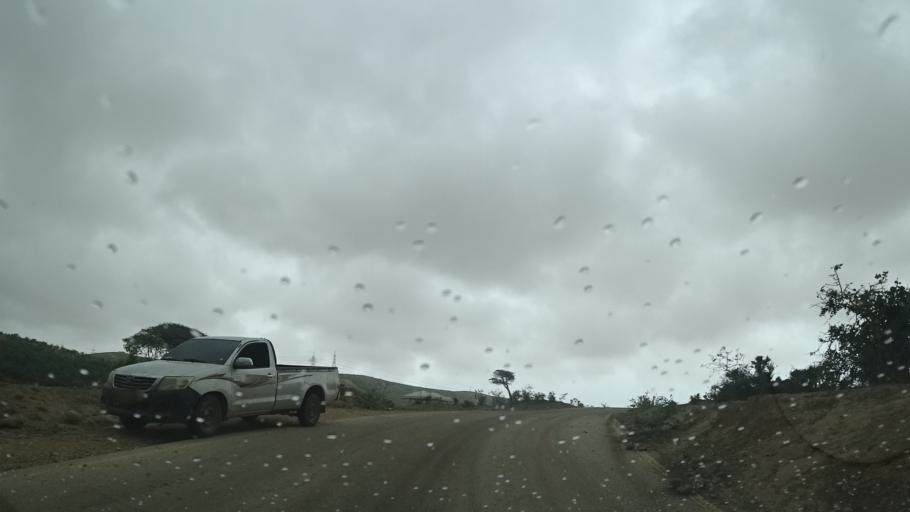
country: OM
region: Zufar
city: Salalah
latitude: 17.0950
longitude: 54.3333
